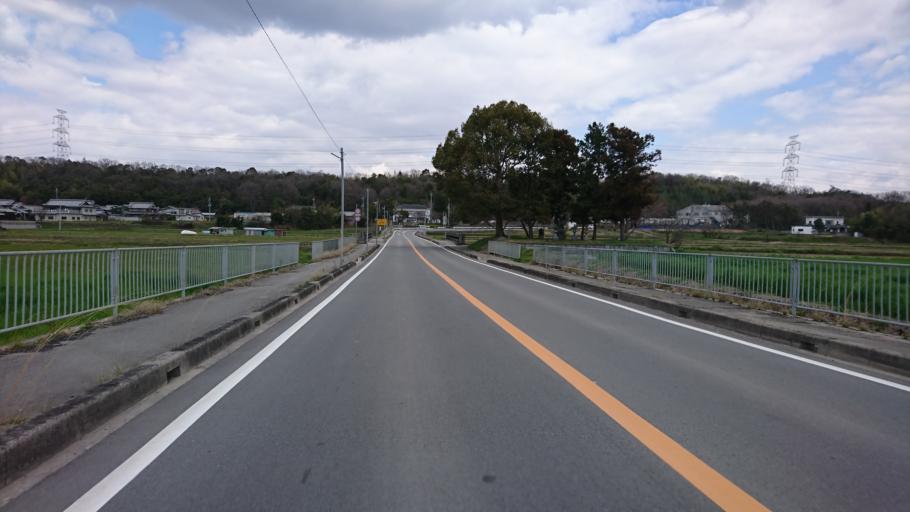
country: JP
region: Hyogo
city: Miki
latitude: 34.7660
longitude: 134.9524
